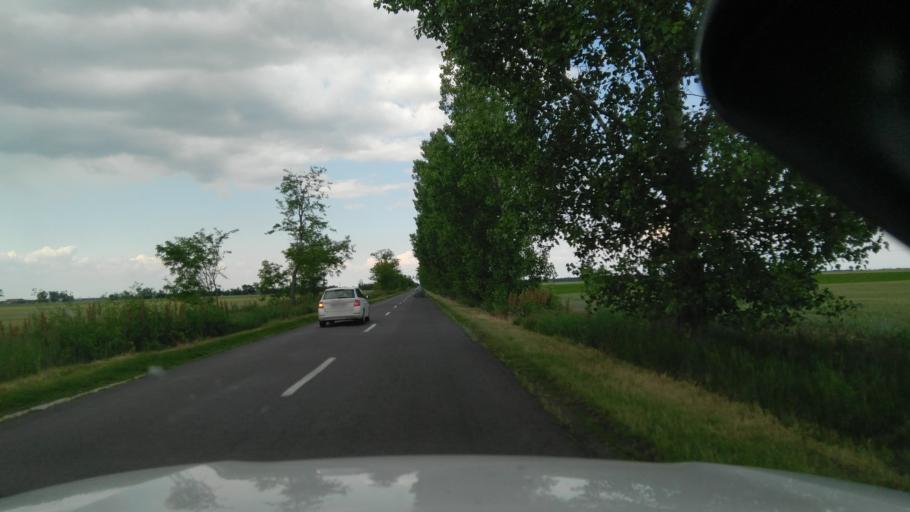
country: HU
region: Bekes
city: Magyarbanhegyes
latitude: 46.4577
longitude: 21.0024
